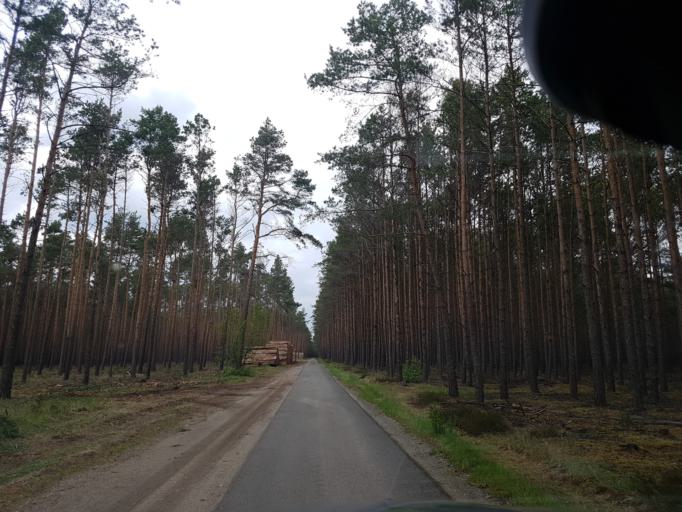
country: DE
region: Brandenburg
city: Crinitz
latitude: 51.6768
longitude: 13.7808
